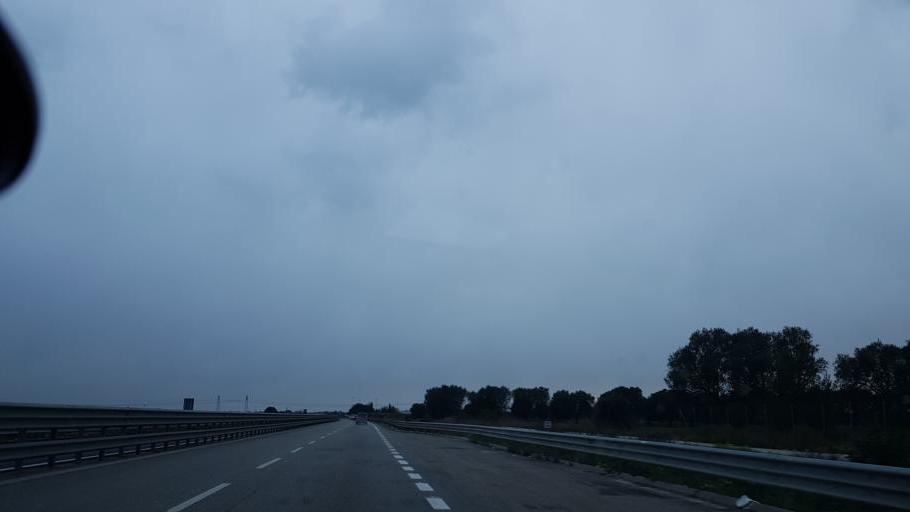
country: IT
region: Apulia
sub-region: Provincia di Brindisi
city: Mesagne
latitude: 40.5848
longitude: 17.8492
